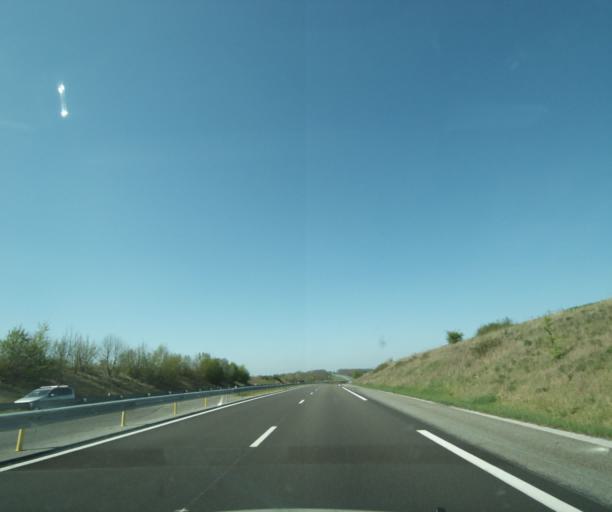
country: FR
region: Bourgogne
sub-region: Departement de la Nievre
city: Neuvy-sur-Loire
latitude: 47.5266
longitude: 2.9084
